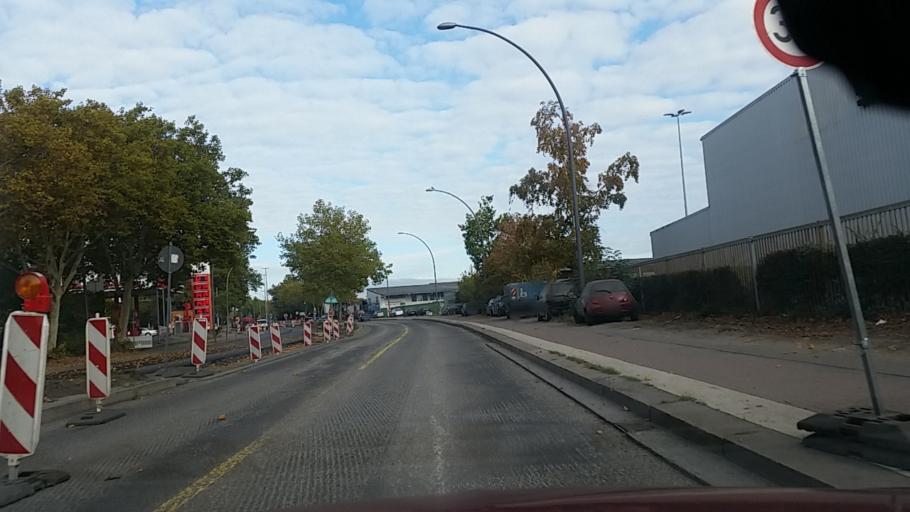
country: DE
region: Hamburg
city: Marienthal
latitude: 53.5368
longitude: 10.0836
